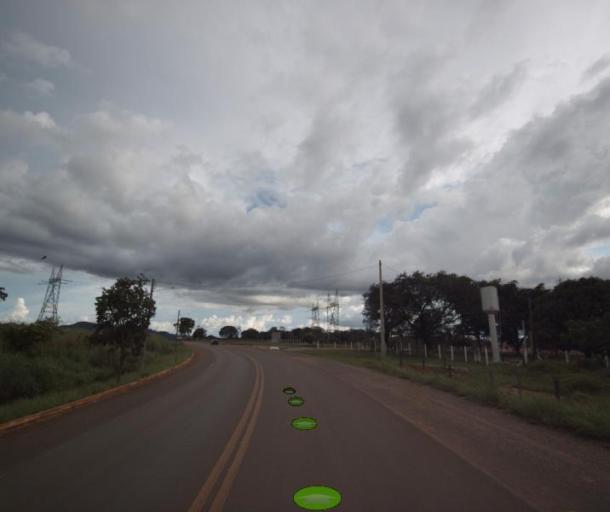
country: BR
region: Goias
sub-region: Niquelandia
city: Niquelandia
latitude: -14.4715
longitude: -48.4883
